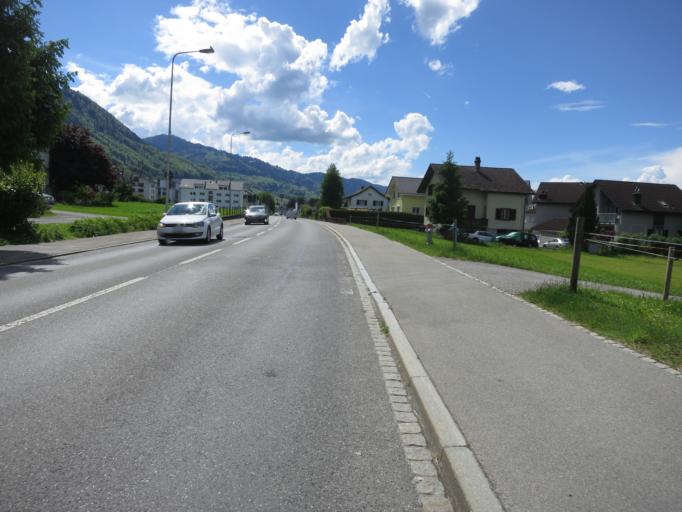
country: CH
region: Schwyz
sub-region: Bezirk March
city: Schubelbach
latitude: 47.1753
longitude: 8.9390
